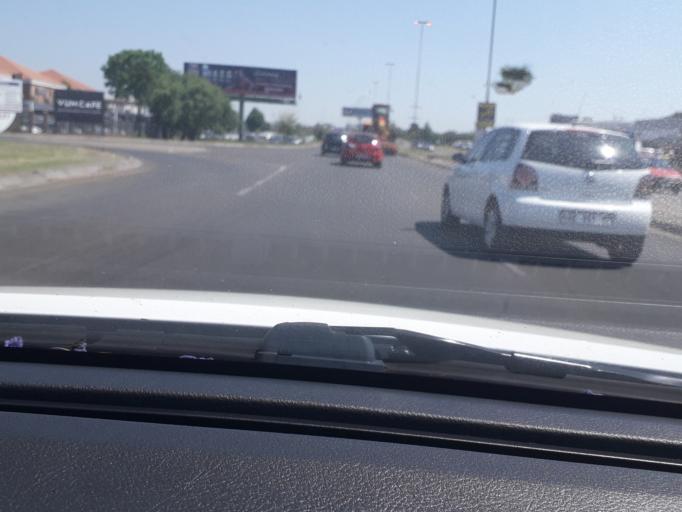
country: ZA
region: Gauteng
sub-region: Ekurhuleni Metropolitan Municipality
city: Boksburg
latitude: -26.1782
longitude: 28.2432
